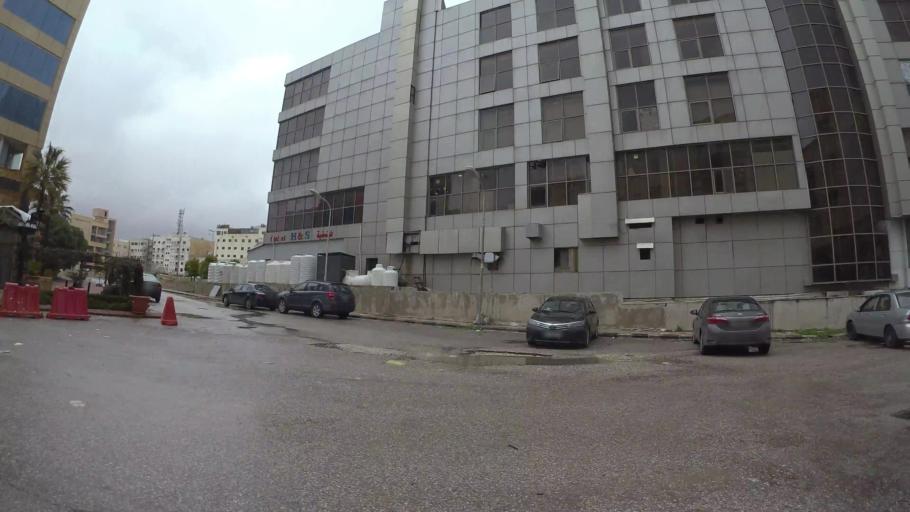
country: JO
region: Amman
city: Wadi as Sir
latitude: 31.9545
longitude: 35.8551
